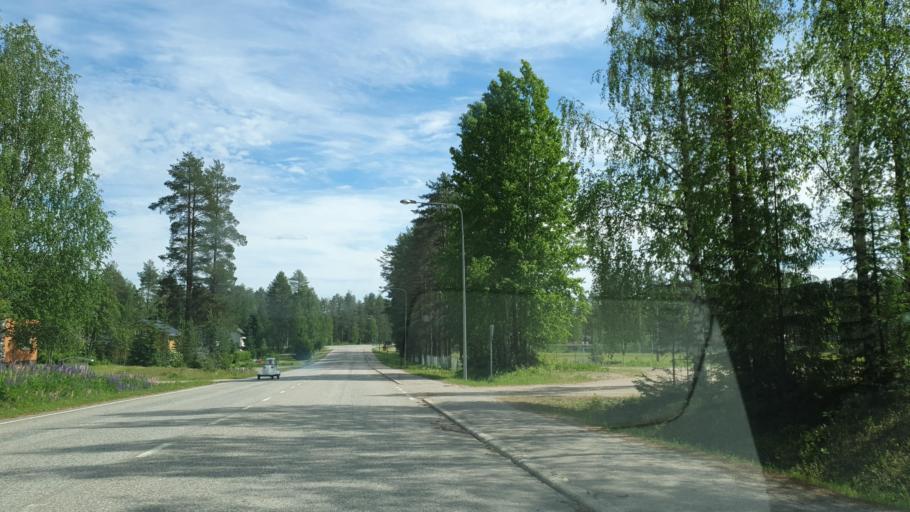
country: FI
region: Kainuu
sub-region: Kehys-Kainuu
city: Hyrynsalmi
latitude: 64.6823
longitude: 28.4701
